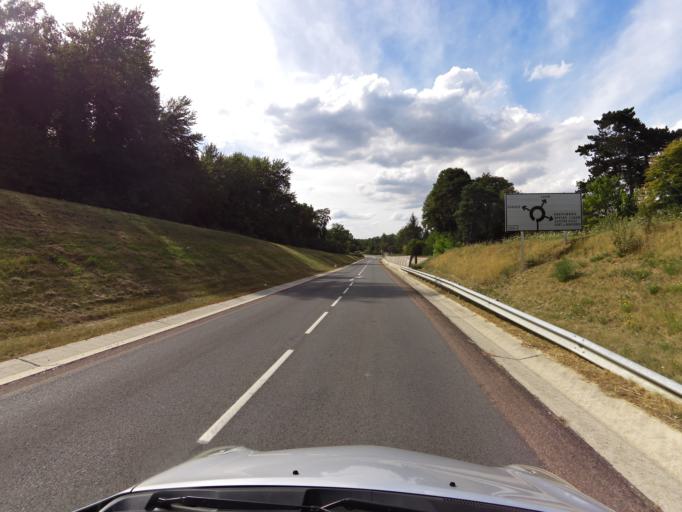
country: FR
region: Picardie
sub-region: Departement de l'Aisne
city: Bruyeres-et-Montberault
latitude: 49.5233
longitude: 3.6625
